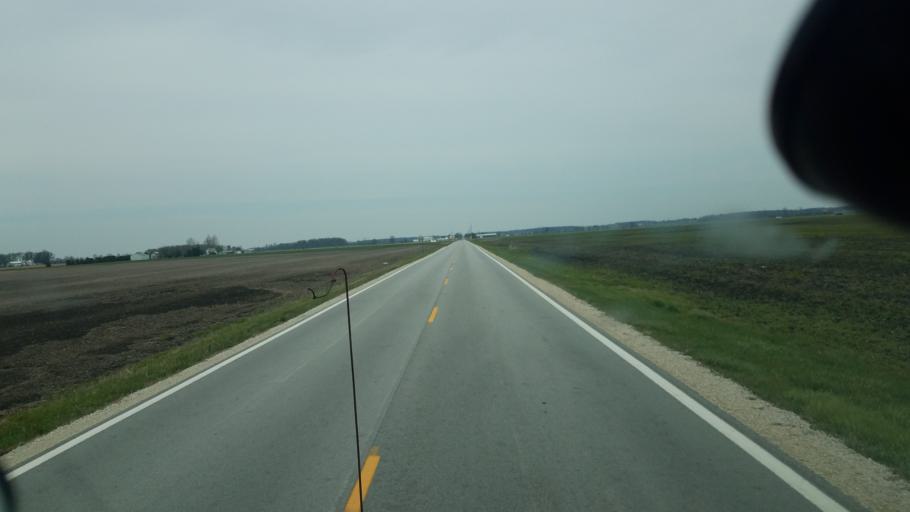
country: US
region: Ohio
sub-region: Wyandot County
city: Carey
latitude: 40.9954
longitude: -83.4778
